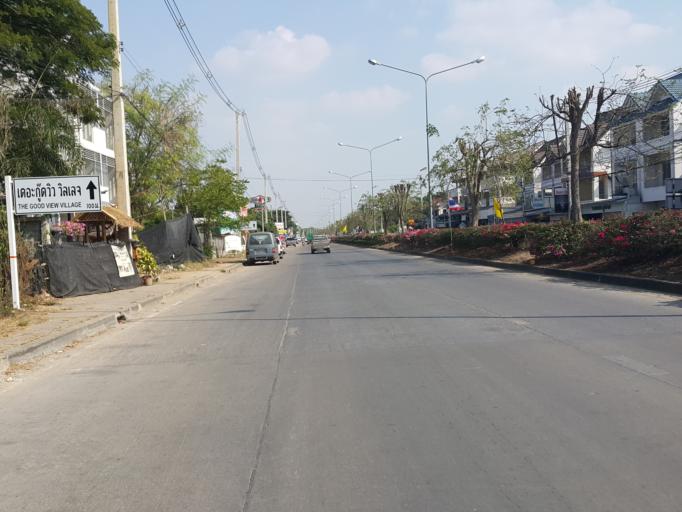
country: TH
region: Chiang Mai
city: Chiang Mai
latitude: 18.7494
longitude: 98.9416
